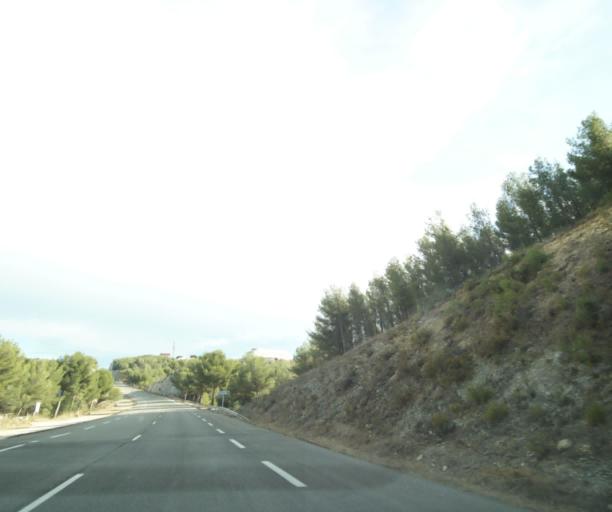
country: FR
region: Provence-Alpes-Cote d'Azur
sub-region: Departement des Bouches-du-Rhone
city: Sausset-les-Pins
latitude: 43.3427
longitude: 5.0948
